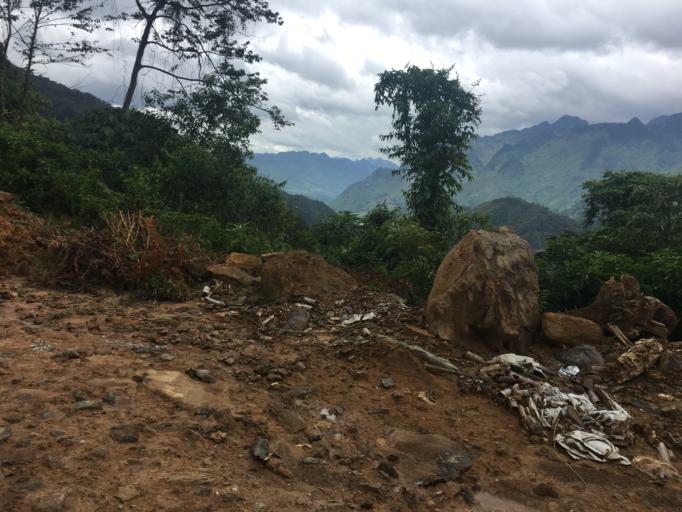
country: VN
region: Ha Giang
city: Thi Tran Tam Son
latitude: 22.9921
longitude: 105.0684
